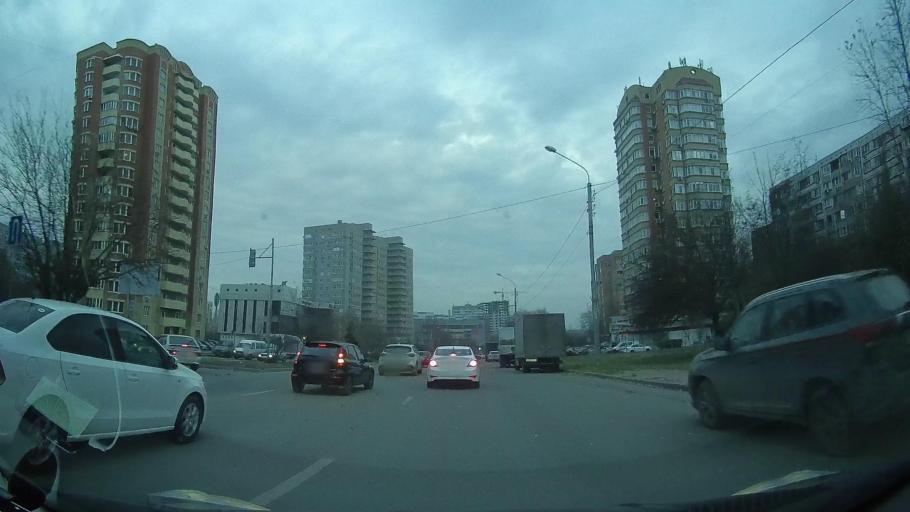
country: RU
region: Rostov
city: Severnyy
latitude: 47.2951
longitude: 39.7096
